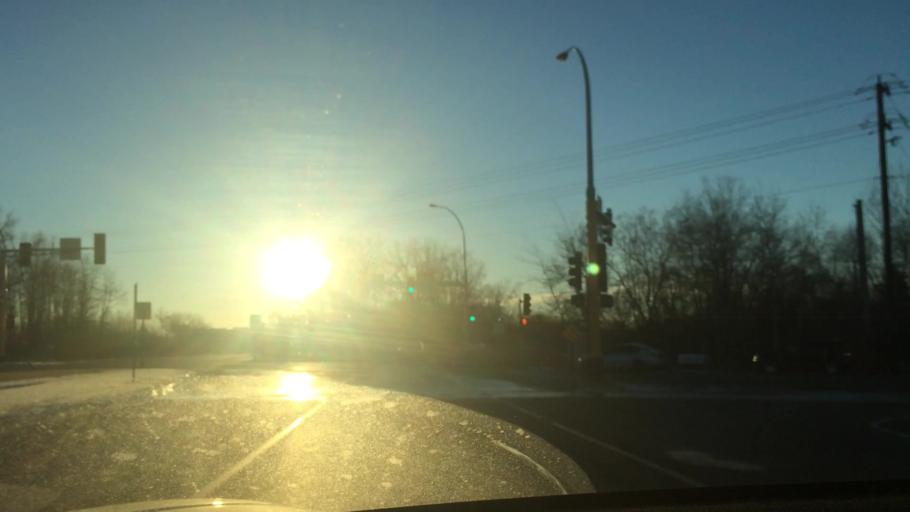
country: US
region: Minnesota
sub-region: Anoka County
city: Lexington
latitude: 45.1292
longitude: -93.1838
